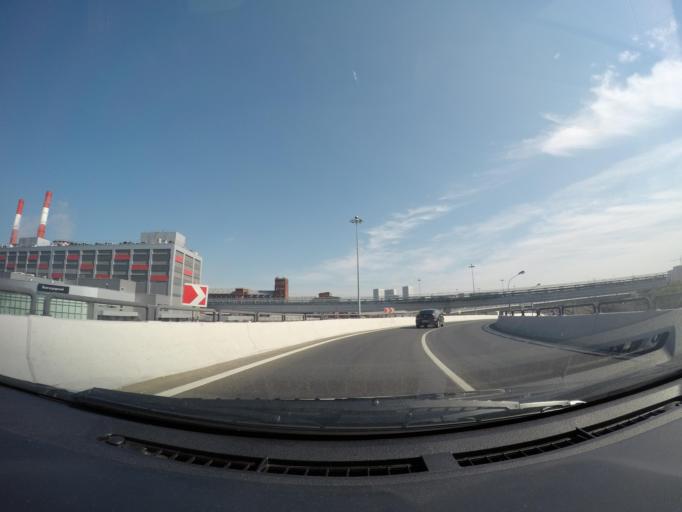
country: RU
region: Moscow
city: Taganskiy
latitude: 55.7202
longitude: 37.7029
